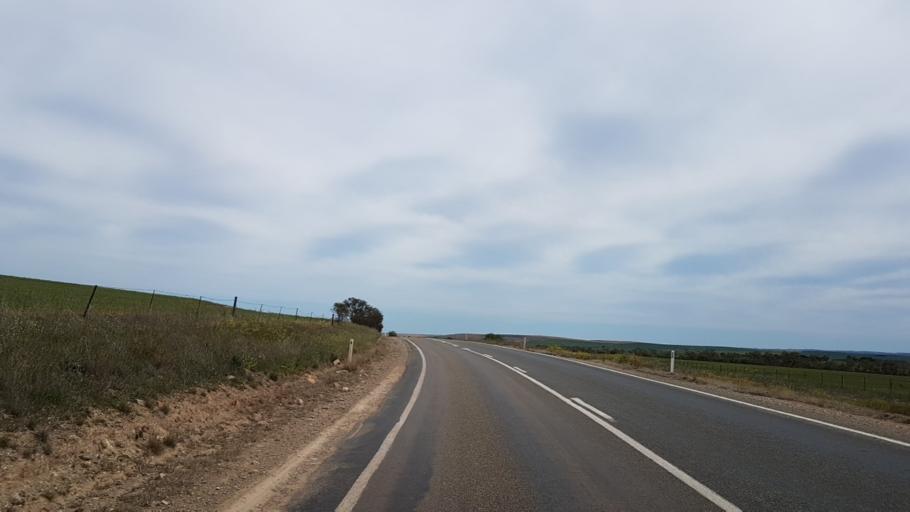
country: AU
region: South Australia
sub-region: Northern Areas
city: Jamestown
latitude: -33.2080
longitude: 138.4292
